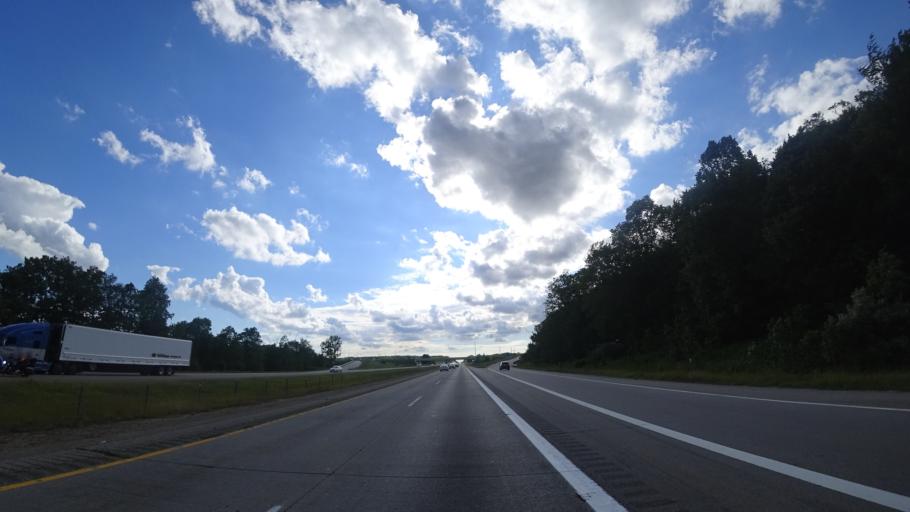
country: US
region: Michigan
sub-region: Kent County
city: Lowell
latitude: 42.8789
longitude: -85.3662
